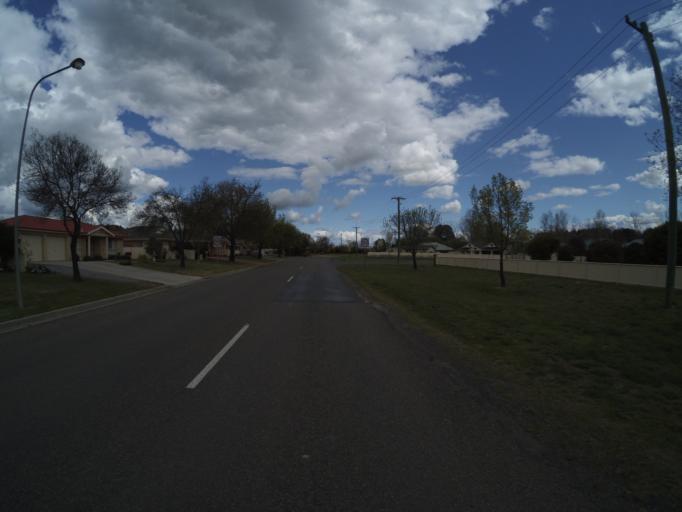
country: AU
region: New South Wales
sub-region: Yass Valley
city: Yass
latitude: -34.8570
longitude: 148.9187
